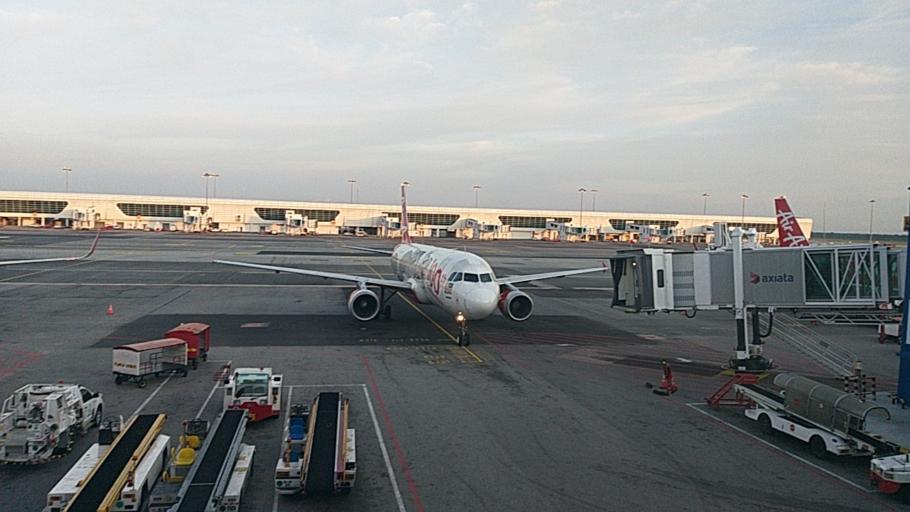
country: MY
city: Sungai Pelek New Village
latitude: 2.7406
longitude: 101.6842
